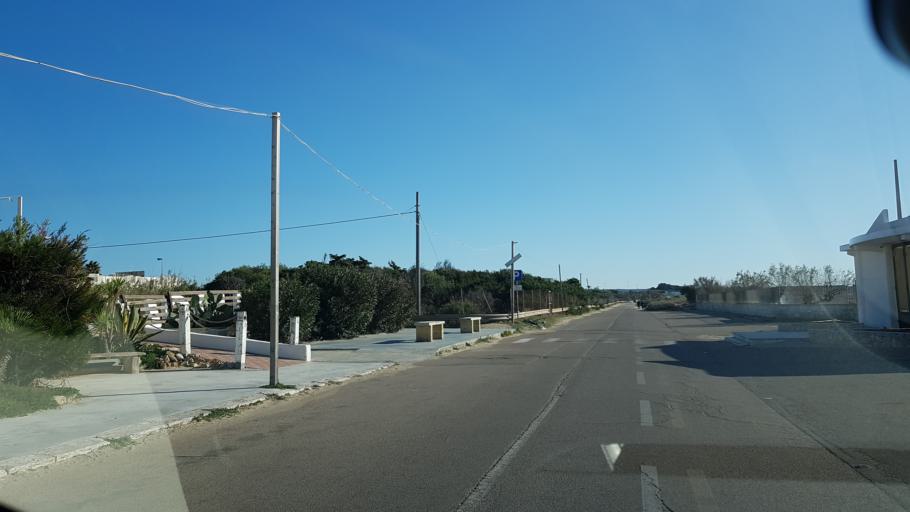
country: IT
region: Apulia
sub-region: Provincia di Lecce
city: Gallipoli
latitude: 40.0372
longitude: 18.0147
